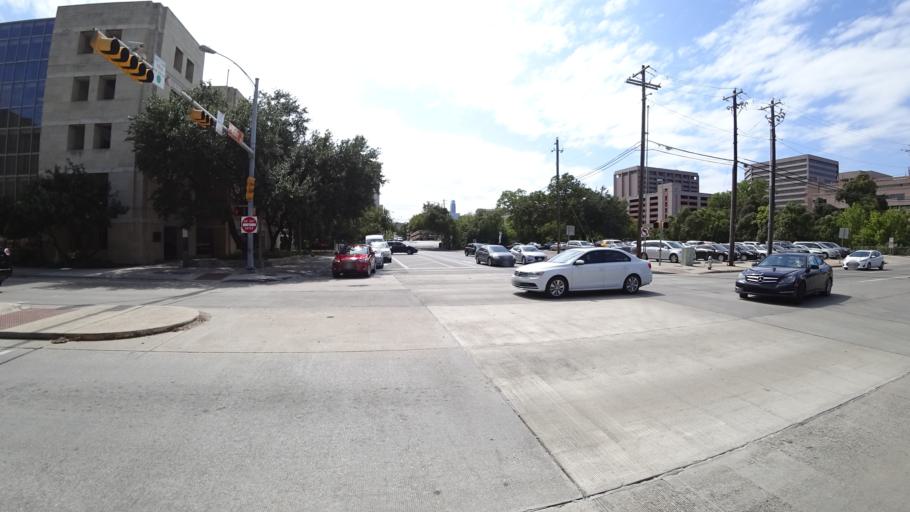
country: US
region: Texas
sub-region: Travis County
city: Austin
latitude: 30.2797
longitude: -97.7344
